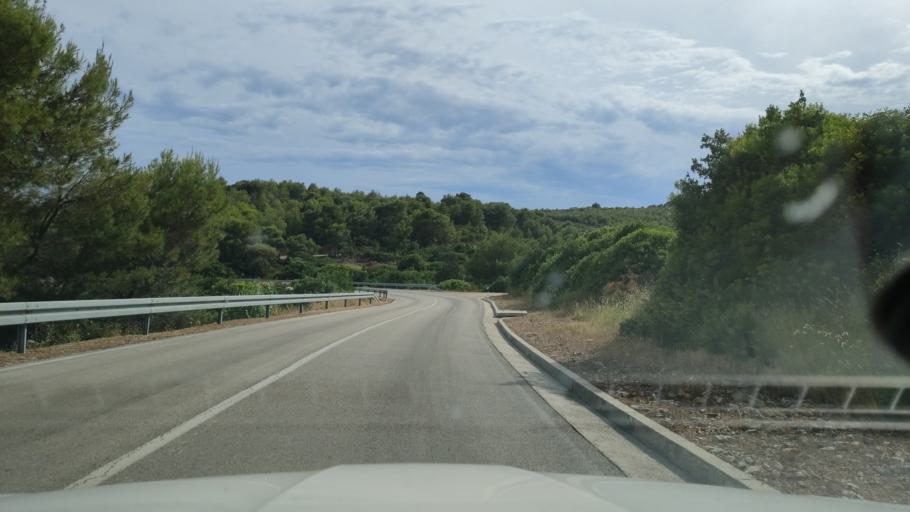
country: HR
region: Splitsko-Dalmatinska
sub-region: Grad Vis
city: Vis
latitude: 43.0342
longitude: 16.2020
